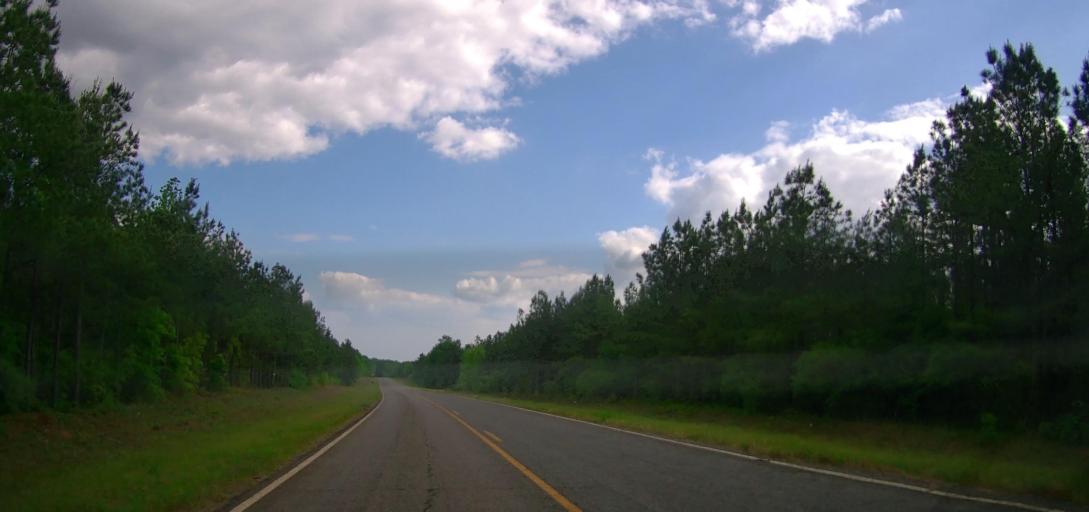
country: US
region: Georgia
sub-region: Johnson County
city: Wrightsville
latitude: 32.7491
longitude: -82.9257
